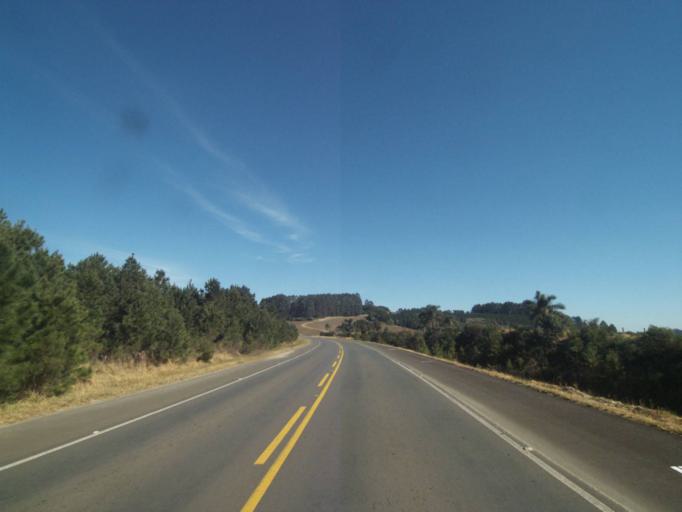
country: BR
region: Parana
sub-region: Tibagi
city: Tibagi
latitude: -24.8084
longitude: -50.4783
